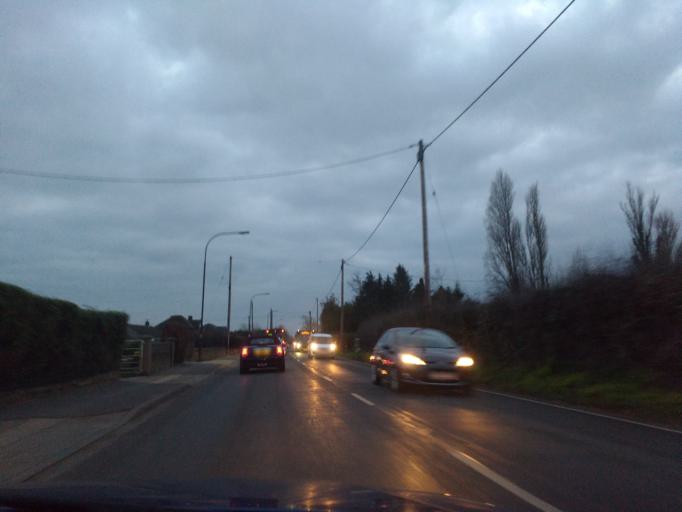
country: GB
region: England
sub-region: Isle of Wight
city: Northwood
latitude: 50.7367
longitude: -1.3072
